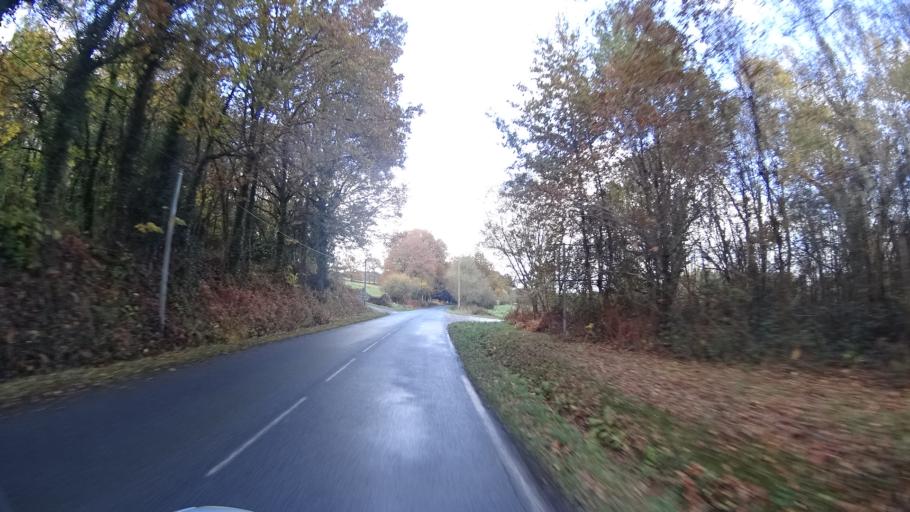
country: FR
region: Brittany
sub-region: Departement du Morbihan
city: Saint-Jean-la-Poterie
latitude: 47.6406
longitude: -2.1134
